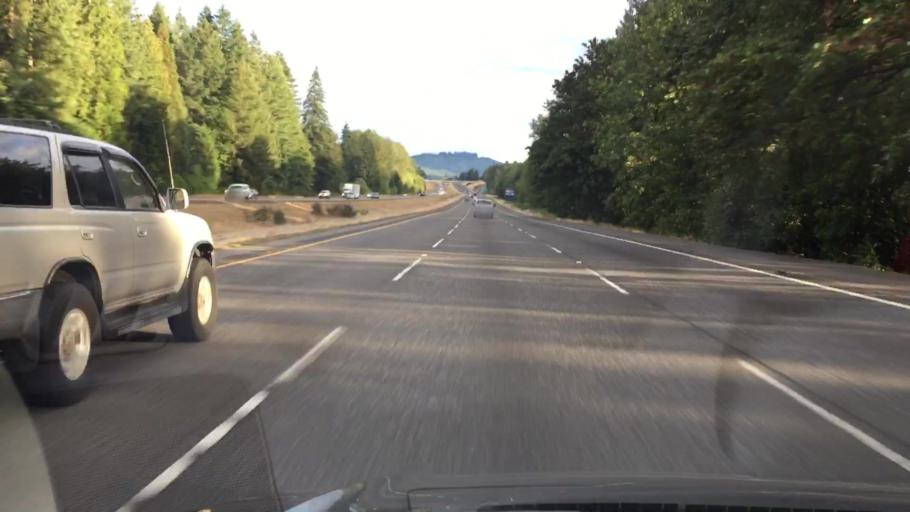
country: US
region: Washington
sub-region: Cowlitz County
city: Castle Rock
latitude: 46.2984
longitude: -122.9103
